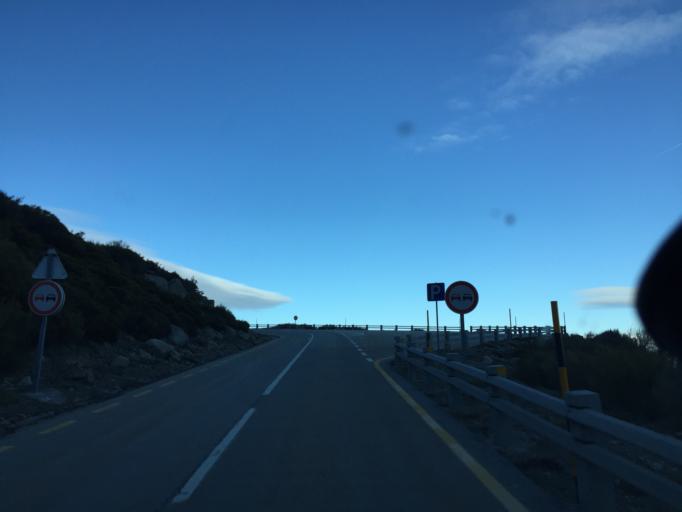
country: PT
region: Castelo Branco
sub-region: Covilha
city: Covilha
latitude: 40.3215
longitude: -7.5883
